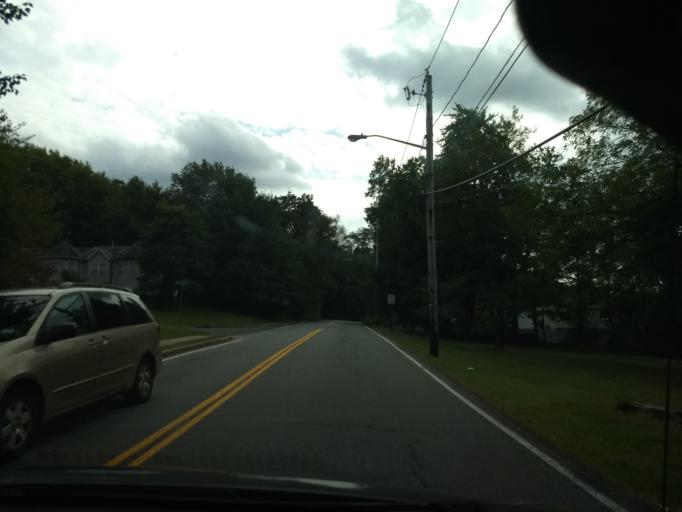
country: US
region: New York
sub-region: Rockland County
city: Spring Valley
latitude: 41.1013
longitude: -74.0427
